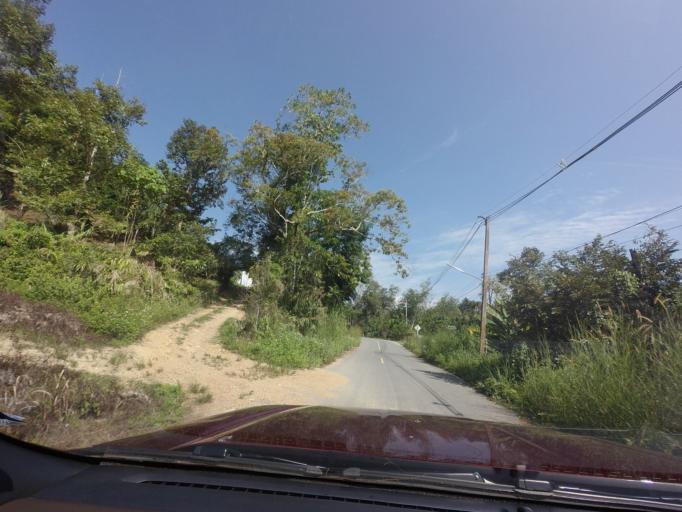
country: TH
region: Yala
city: Than To
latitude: 6.0083
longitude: 101.2246
